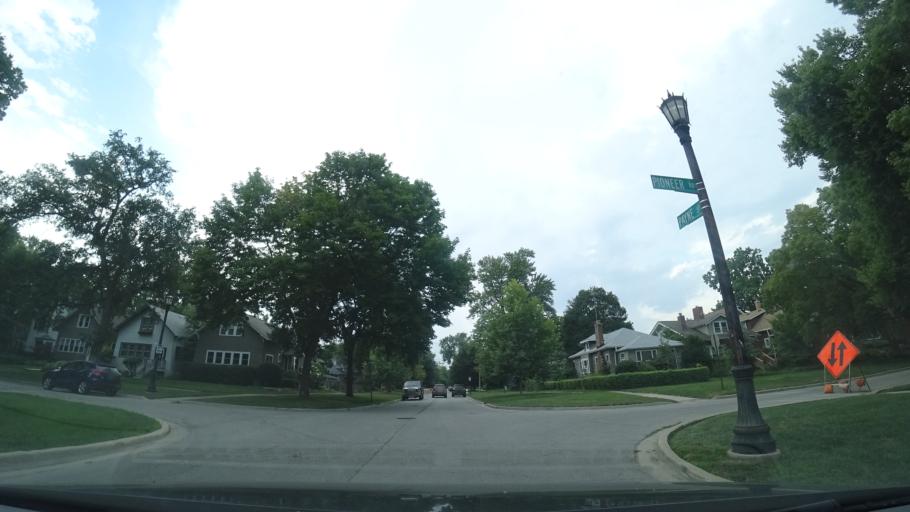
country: US
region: Illinois
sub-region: Cook County
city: Evanston
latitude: 42.0568
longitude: -87.7057
